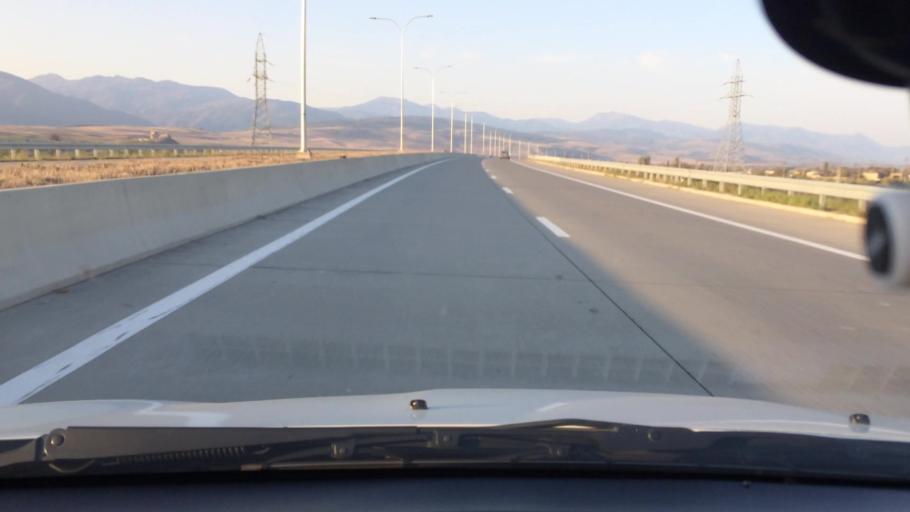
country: GE
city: Agara
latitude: 42.0354
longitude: 43.8475
